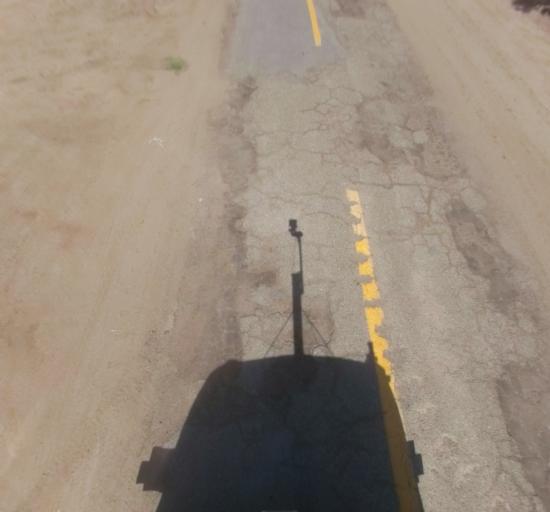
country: US
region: California
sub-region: Madera County
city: Chowchilla
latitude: 37.0326
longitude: -120.3614
